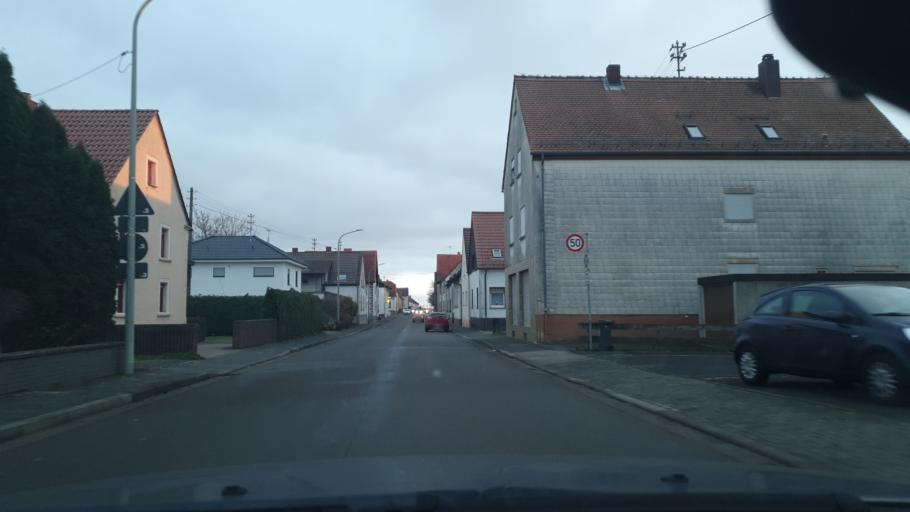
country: DE
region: Rheinland-Pfalz
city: Martinshohe
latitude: 49.3638
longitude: 7.4813
